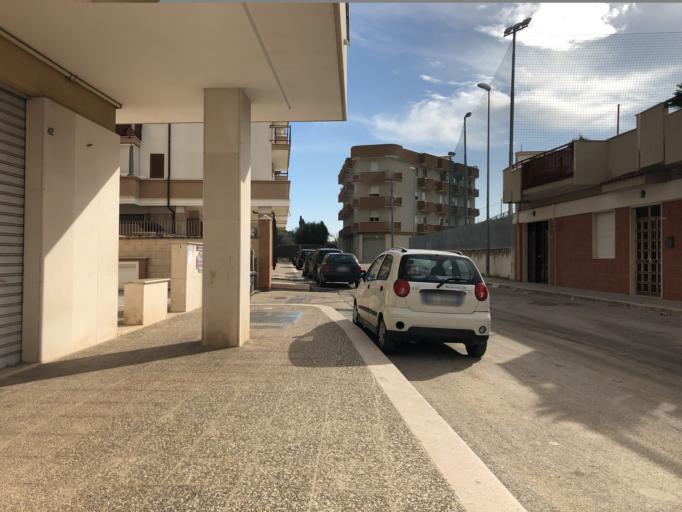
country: IT
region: Apulia
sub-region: Provincia di Barletta - Andria - Trani
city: Andria
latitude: 41.2180
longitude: 16.3047
